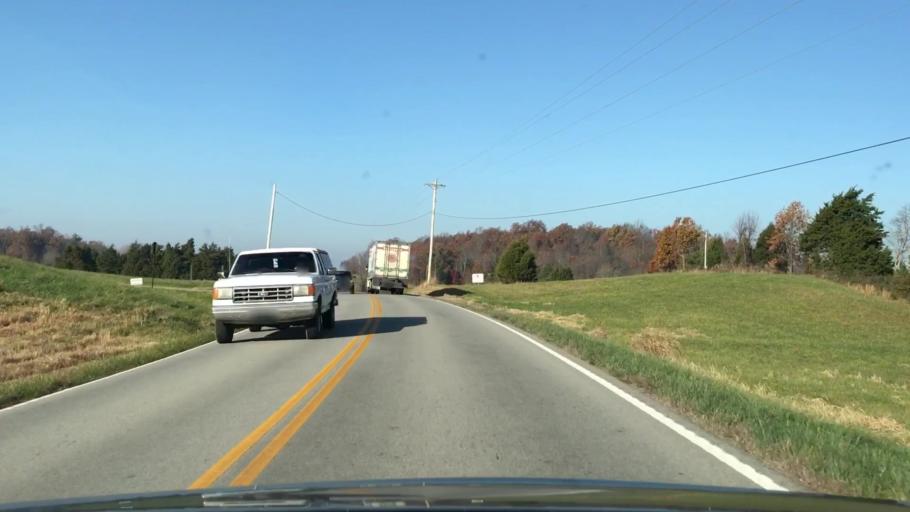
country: US
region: Kentucky
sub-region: Grayson County
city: Leitchfield
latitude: 37.4085
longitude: -86.2574
